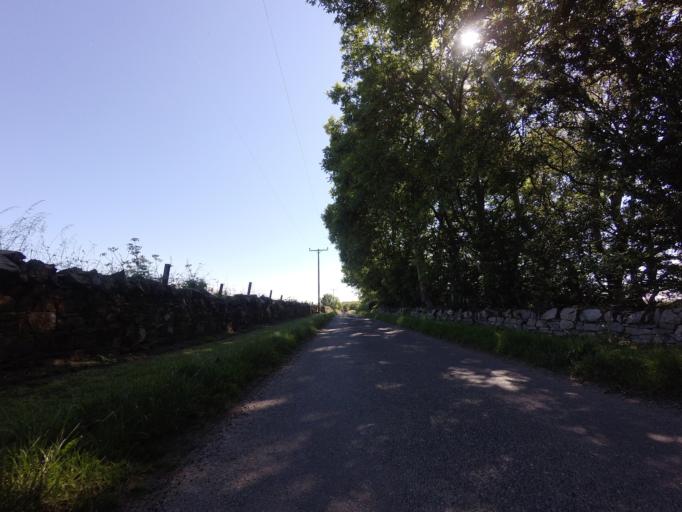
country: GB
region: Scotland
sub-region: Aberdeenshire
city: Macduff
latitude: 57.6550
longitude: -2.5002
